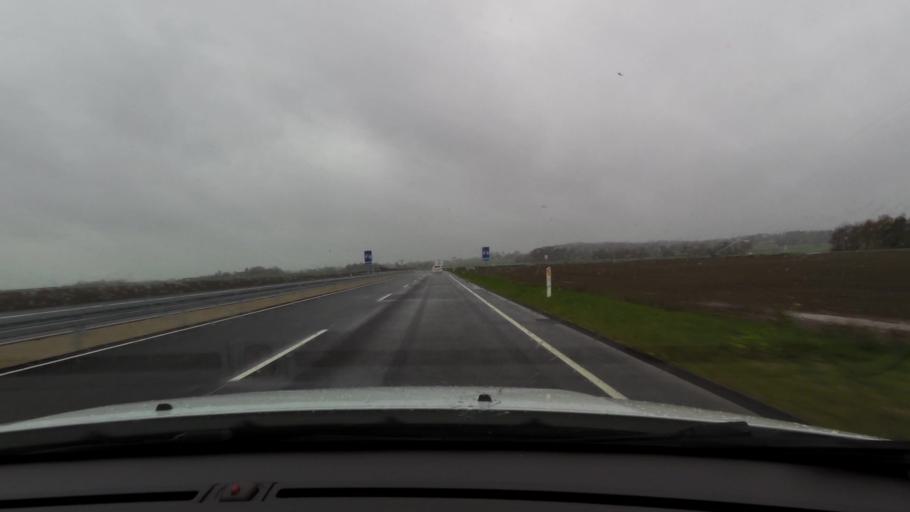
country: DK
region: Capital Region
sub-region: Frederikssund Kommune
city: Skibby
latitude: 55.7932
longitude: 11.9821
